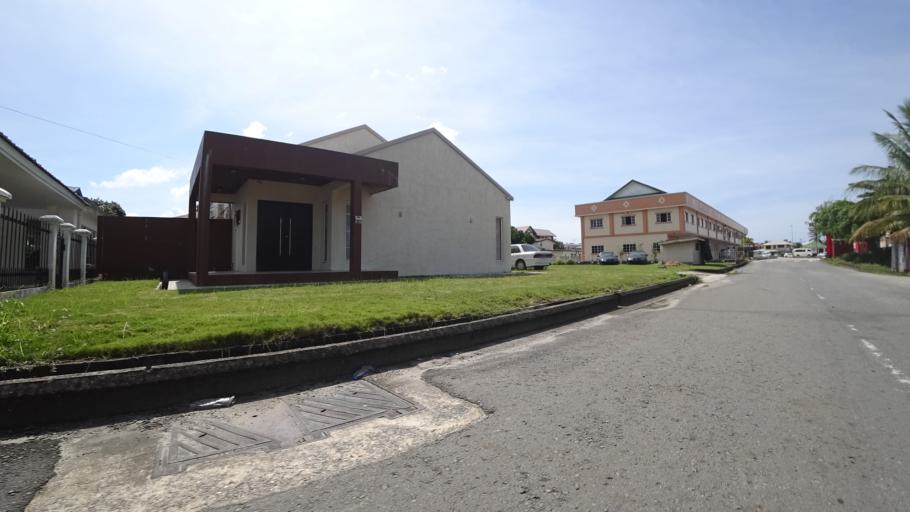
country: BN
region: Brunei and Muara
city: Bandar Seri Begawan
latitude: 4.8912
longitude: 114.8481
